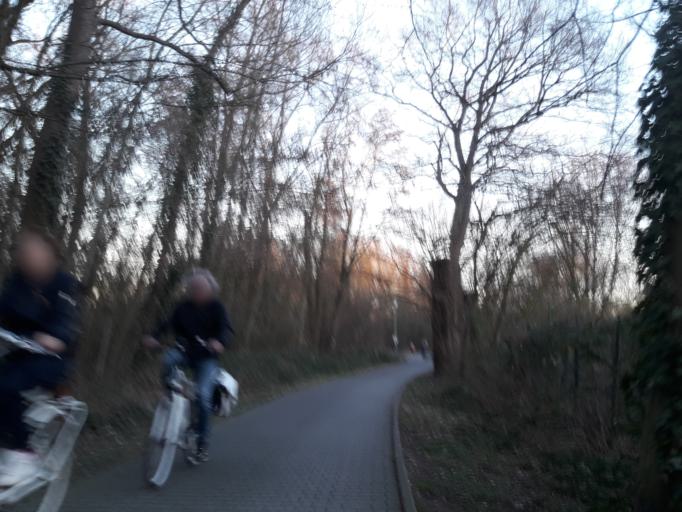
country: DE
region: North Rhine-Westphalia
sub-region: Regierungsbezirk Detmold
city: Paderborn
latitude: 51.7297
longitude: 8.7339
